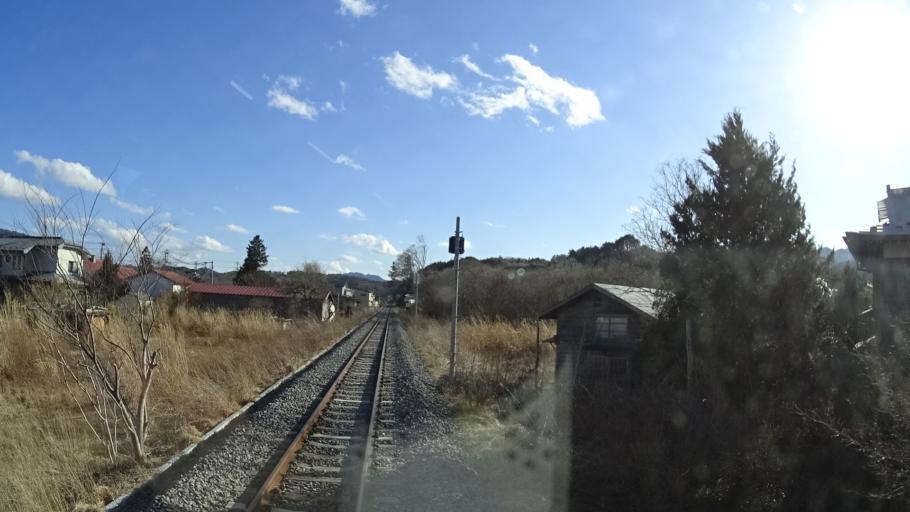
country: JP
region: Iwate
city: Miyako
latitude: 39.5761
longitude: 141.9345
